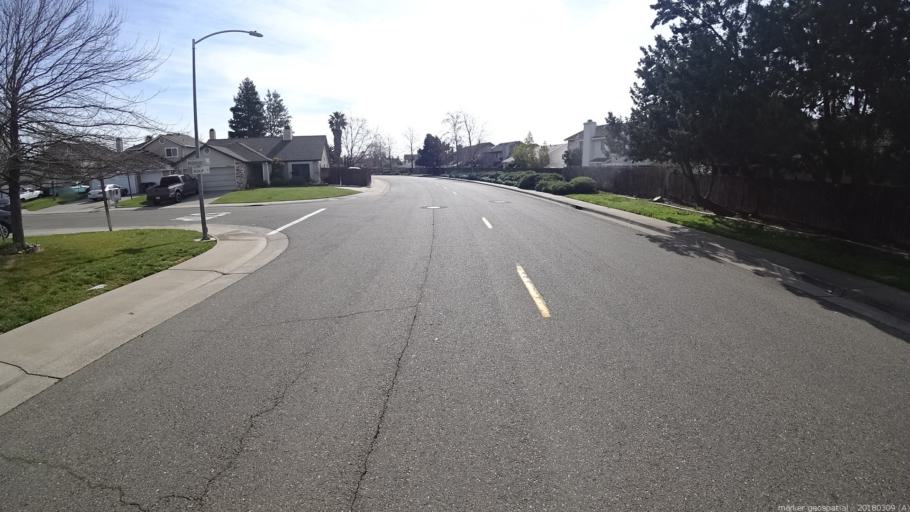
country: US
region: California
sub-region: Sacramento County
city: Florin
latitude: 38.4570
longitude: -121.4015
